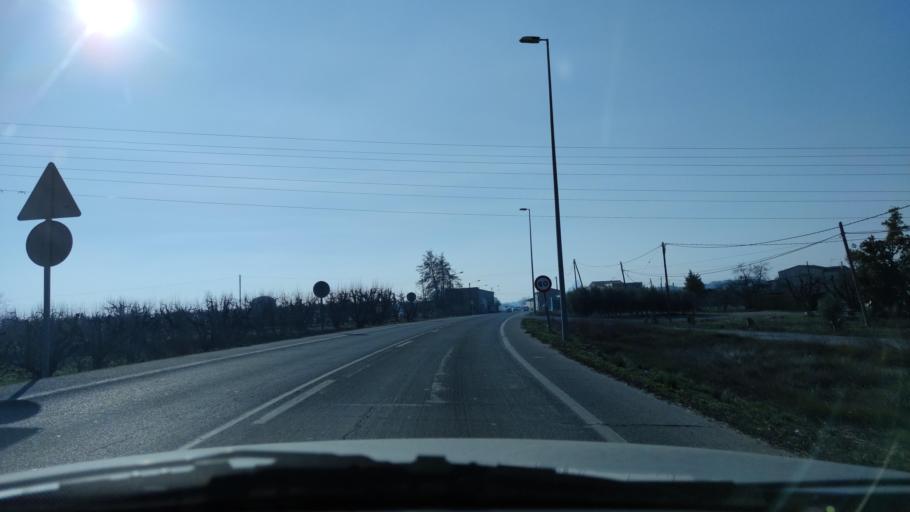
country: ES
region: Catalonia
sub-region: Provincia de Lleida
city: Lleida
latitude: 41.6451
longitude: 0.6356
